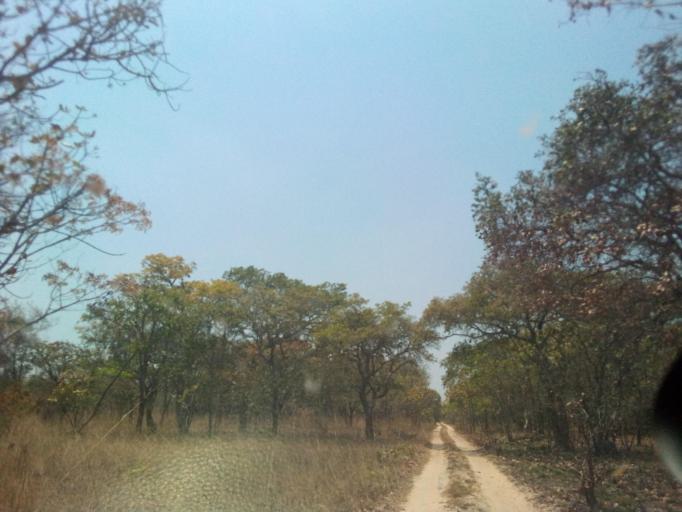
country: ZM
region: Copperbelt
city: Kataba
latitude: -12.2365
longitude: 30.4063
